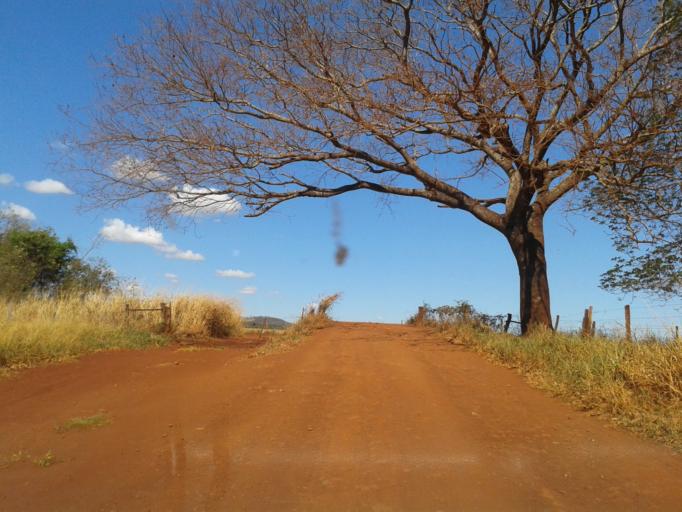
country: BR
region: Minas Gerais
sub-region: Centralina
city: Centralina
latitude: -18.5719
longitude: -49.1361
